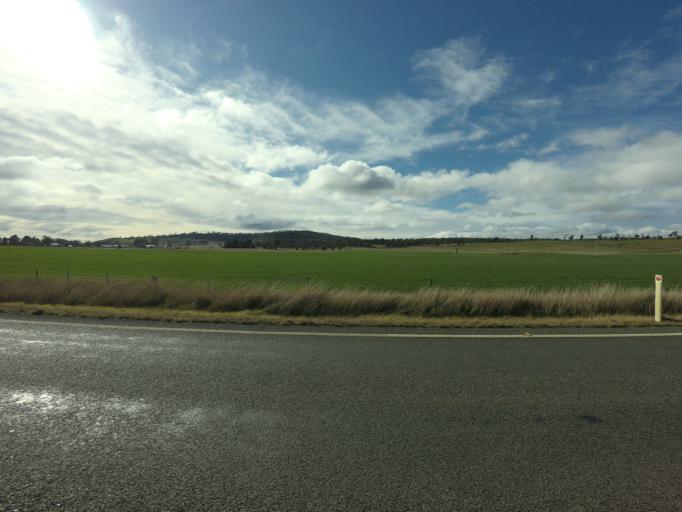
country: AU
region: Tasmania
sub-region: Derwent Valley
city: New Norfolk
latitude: -42.5916
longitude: 146.8810
